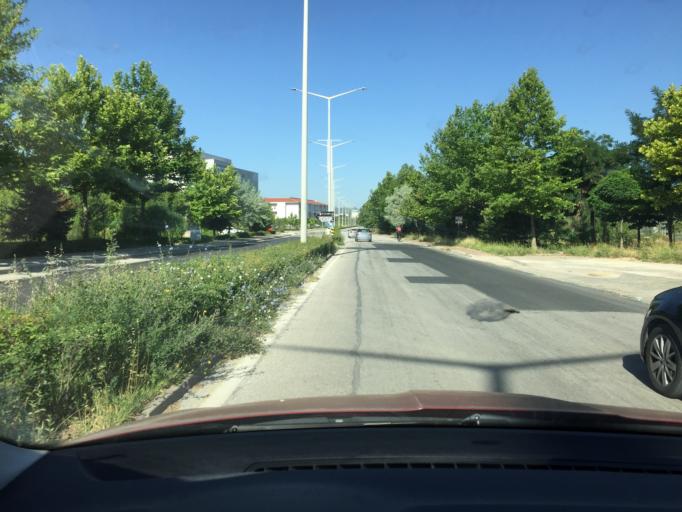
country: TR
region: Eskisehir
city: Eskisehir
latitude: 39.7527
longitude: 30.4817
